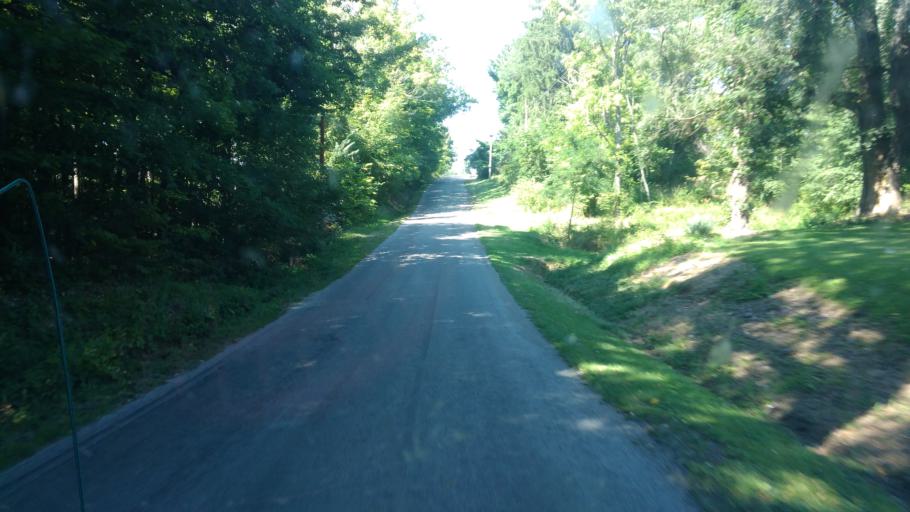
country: US
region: Ohio
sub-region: Ashland County
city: Ashland
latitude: 40.8941
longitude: -82.2687
